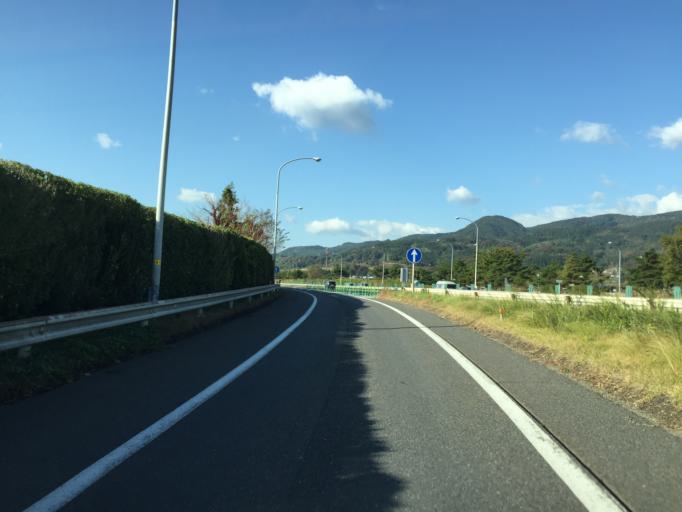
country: JP
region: Fukushima
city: Hobaramachi
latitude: 37.8795
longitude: 140.5299
